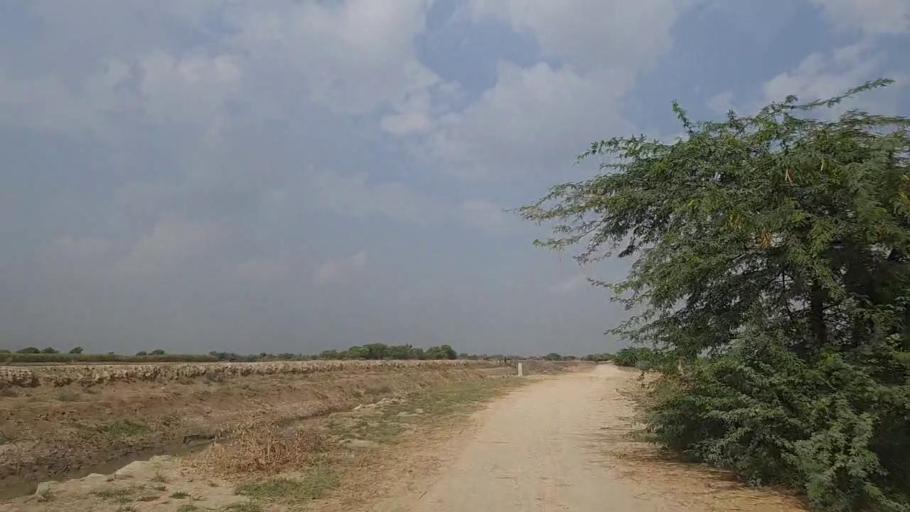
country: PK
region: Sindh
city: Daro Mehar
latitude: 24.6946
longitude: 68.1265
